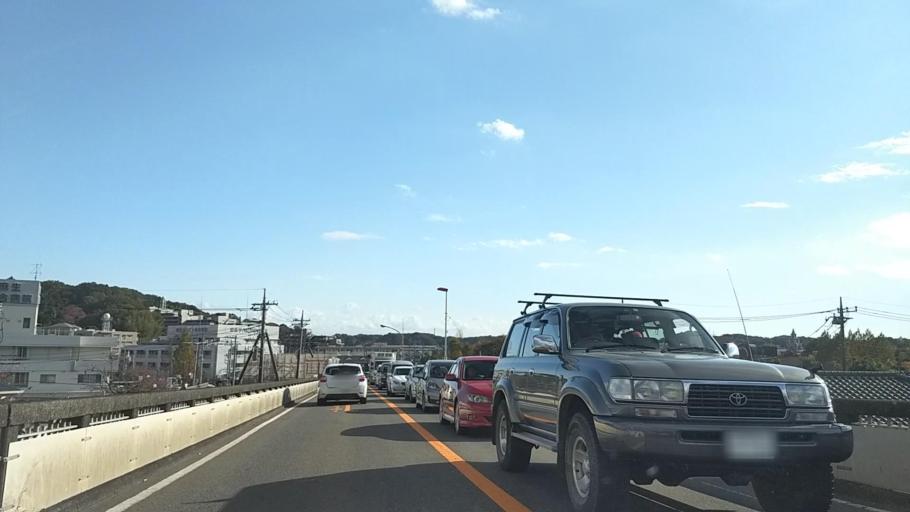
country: JP
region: Tokyo
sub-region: Machida-shi
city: Machida
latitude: 35.5866
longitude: 139.4953
